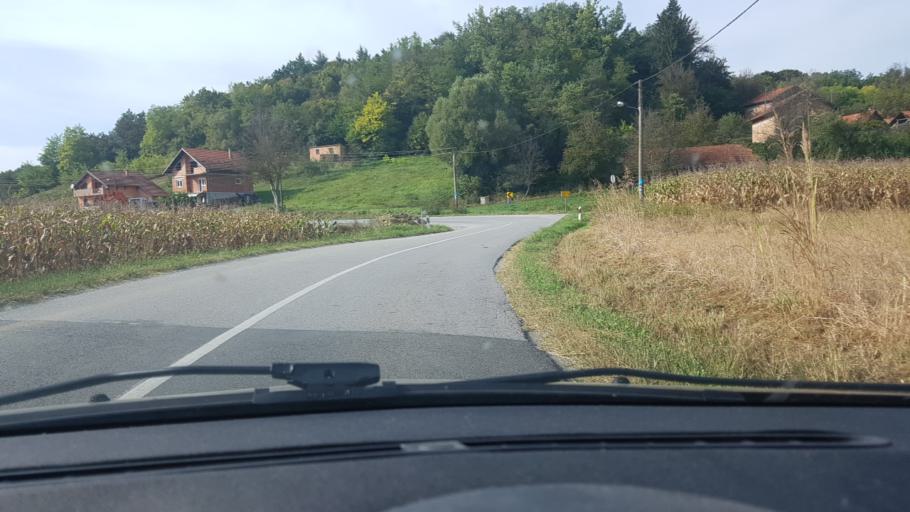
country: HR
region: Krapinsko-Zagorska
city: Mihovljan
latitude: 46.1233
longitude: 15.9880
